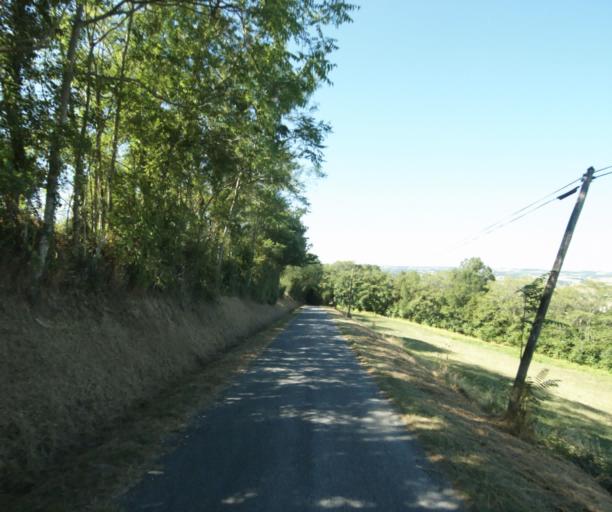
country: FR
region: Midi-Pyrenees
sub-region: Departement de la Haute-Garonne
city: Saint-Felix-Lauragais
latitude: 43.5125
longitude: 1.9345
